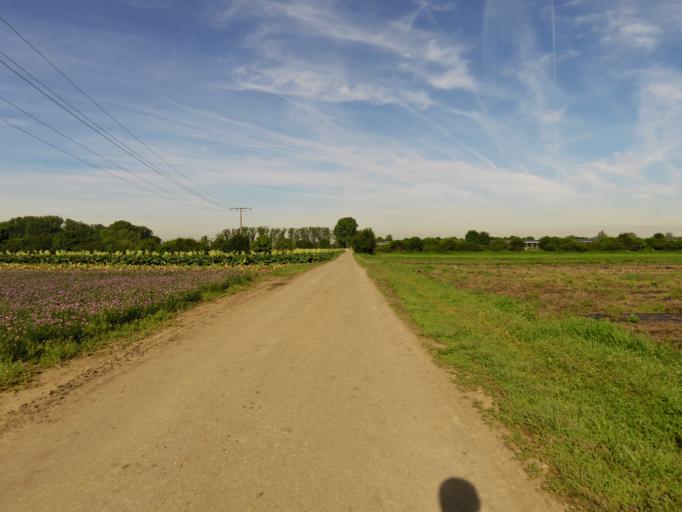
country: DE
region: Hesse
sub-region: Regierungsbezirk Darmstadt
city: Burstadt
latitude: 49.6278
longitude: 8.4782
